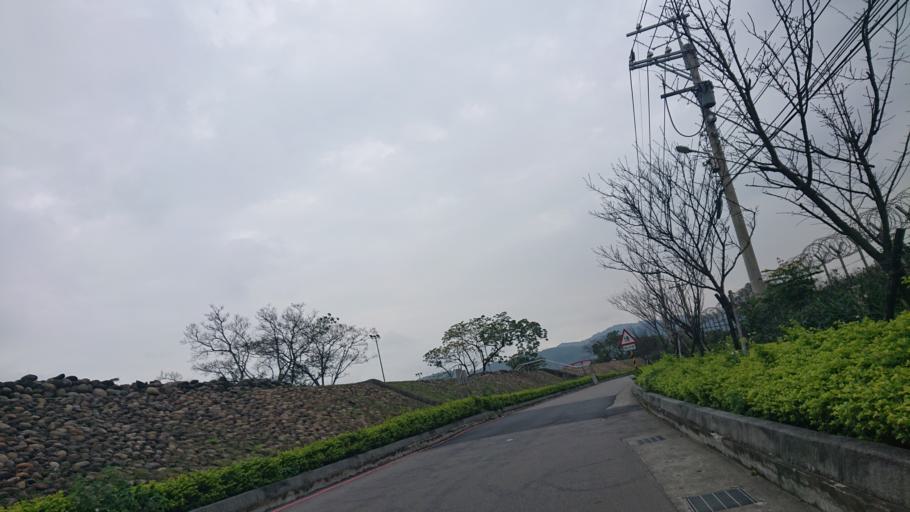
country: TW
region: Taiwan
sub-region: Taoyuan
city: Taoyuan
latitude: 24.9362
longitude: 121.3514
